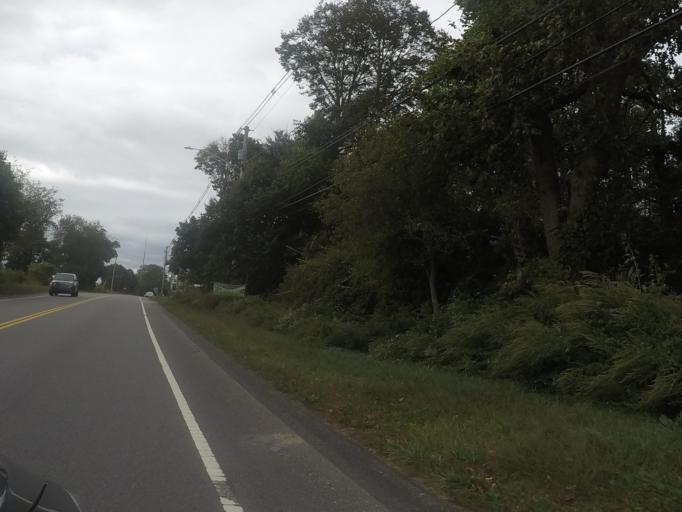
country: US
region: Massachusetts
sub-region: Bristol County
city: Smith Mills
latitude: 41.6769
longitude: -70.9879
